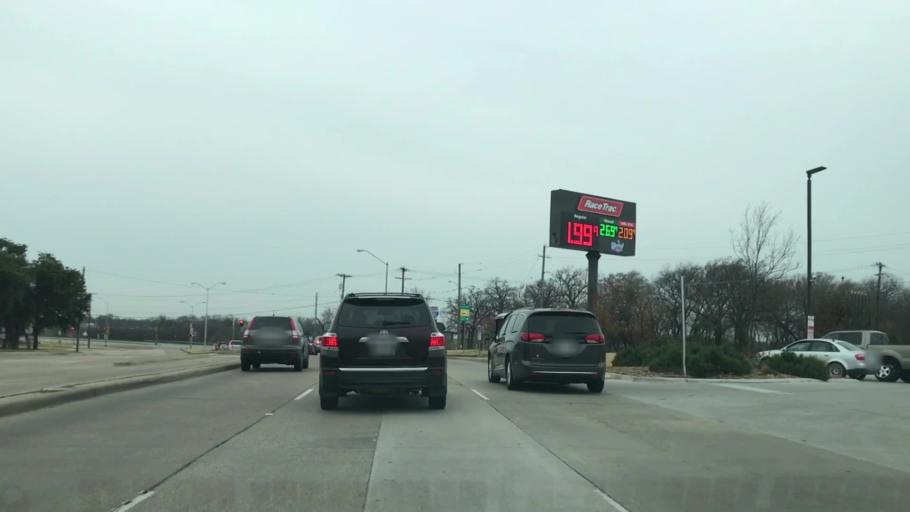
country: US
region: Texas
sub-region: Dallas County
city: University Park
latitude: 32.8513
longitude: -96.8770
